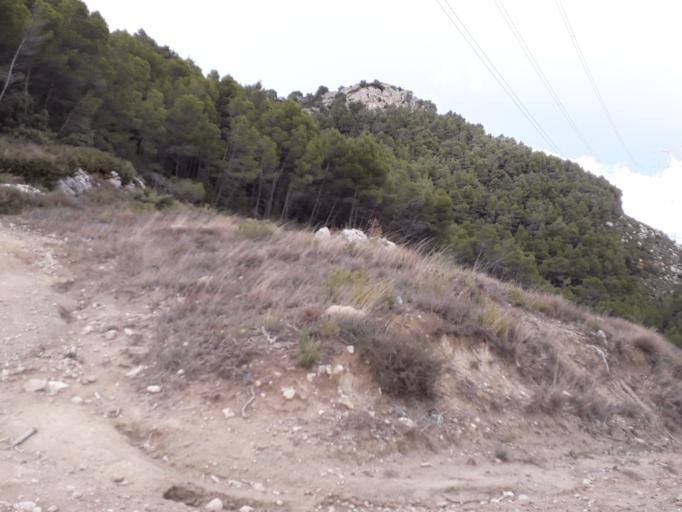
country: ES
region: Catalonia
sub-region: Provincia de Barcelona
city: Sant Marti de Tous
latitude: 41.5149
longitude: 1.4931
